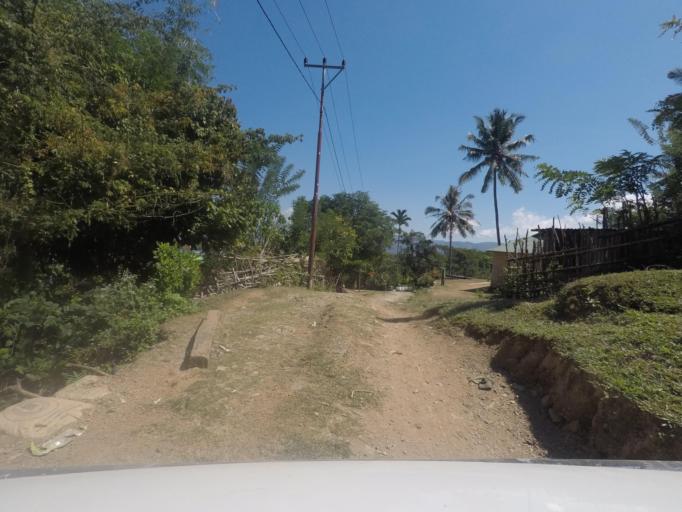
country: TL
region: Ermera
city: Gleno
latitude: -8.7196
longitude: 125.3055
